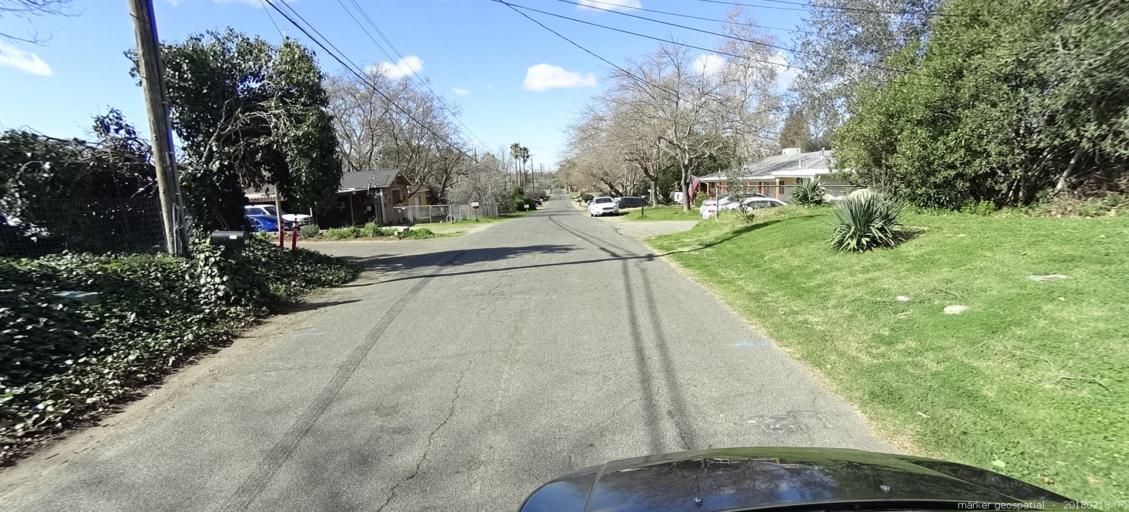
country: US
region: California
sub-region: Sacramento County
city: Orangevale
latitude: 38.6890
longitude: -121.2040
